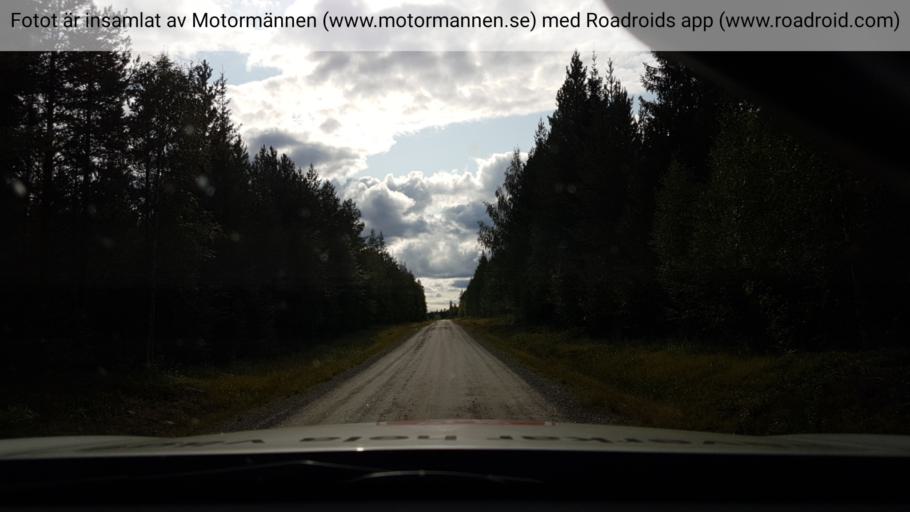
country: SE
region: Vaesterbotten
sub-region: Lycksele Kommun
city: Lycksele
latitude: 64.7101
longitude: 18.8525
